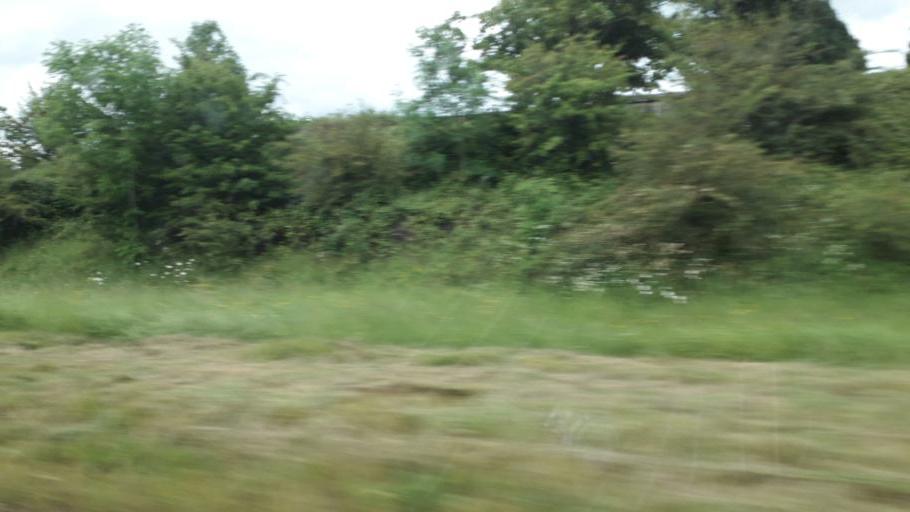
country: IE
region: Leinster
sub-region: County Carlow
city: Bagenalstown
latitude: 52.7359
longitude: -6.9870
